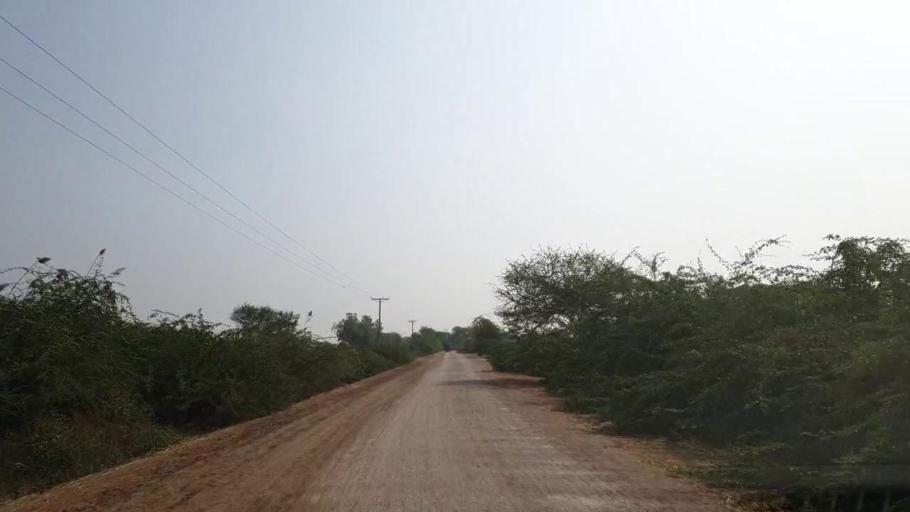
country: PK
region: Sindh
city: Matli
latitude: 24.9969
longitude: 68.5759
